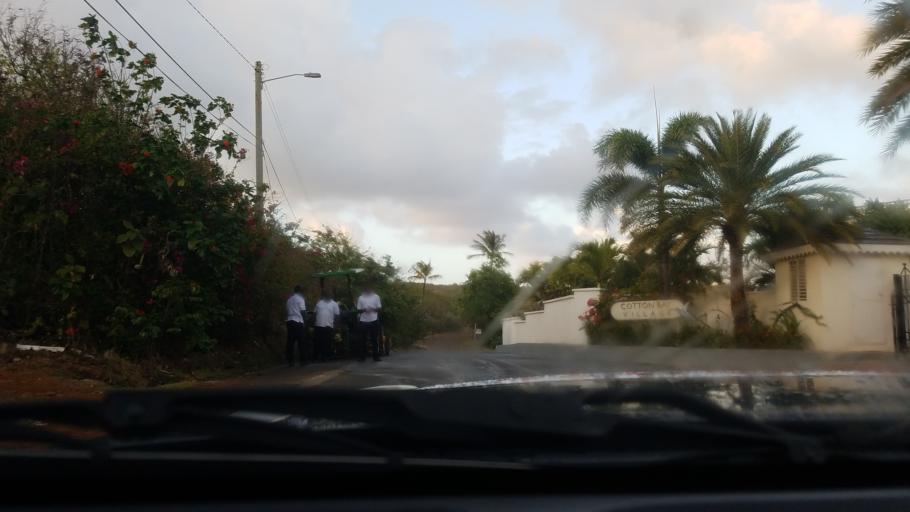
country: LC
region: Gros-Islet
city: Gros Islet
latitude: 14.0911
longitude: -60.9310
